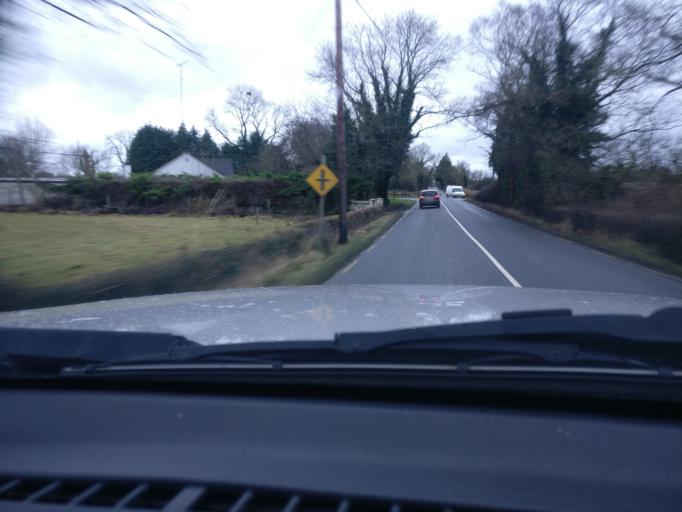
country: IE
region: Leinster
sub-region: An Mhi
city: Longwood
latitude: 53.4827
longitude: -6.8941
